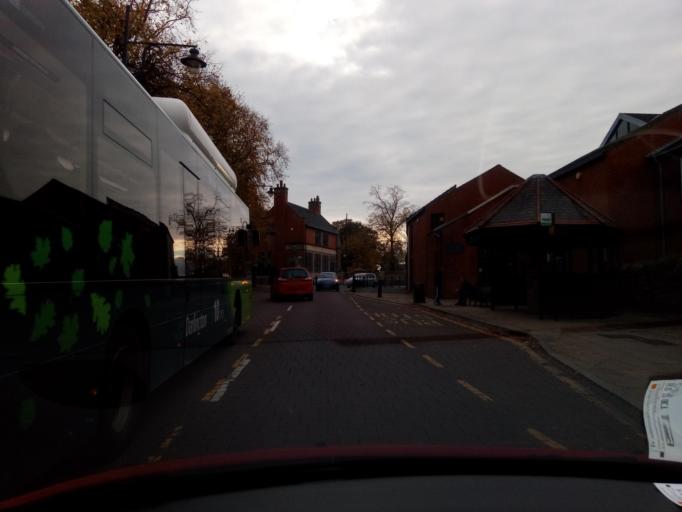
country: GB
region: England
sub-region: County Durham
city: Shildon
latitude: 54.6331
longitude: -1.6480
